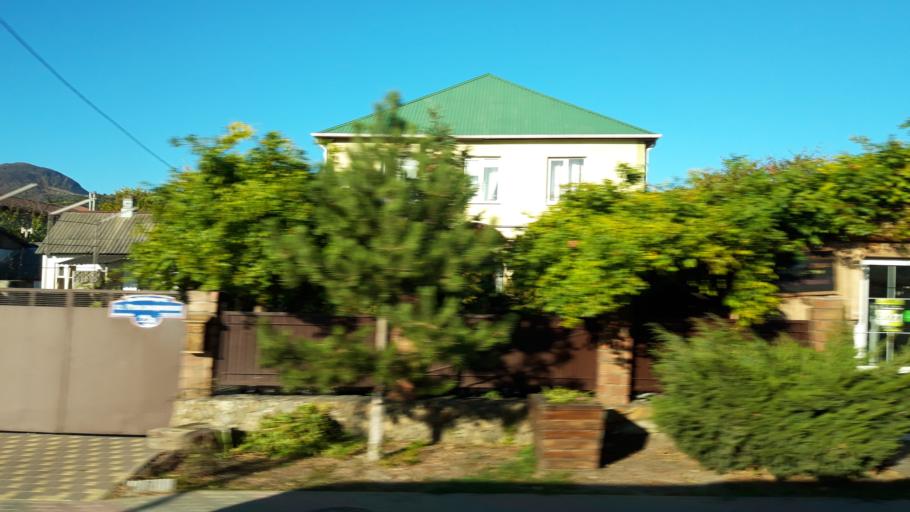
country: RU
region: Krasnodarskiy
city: Kabardinka
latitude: 44.6481
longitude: 37.9494
